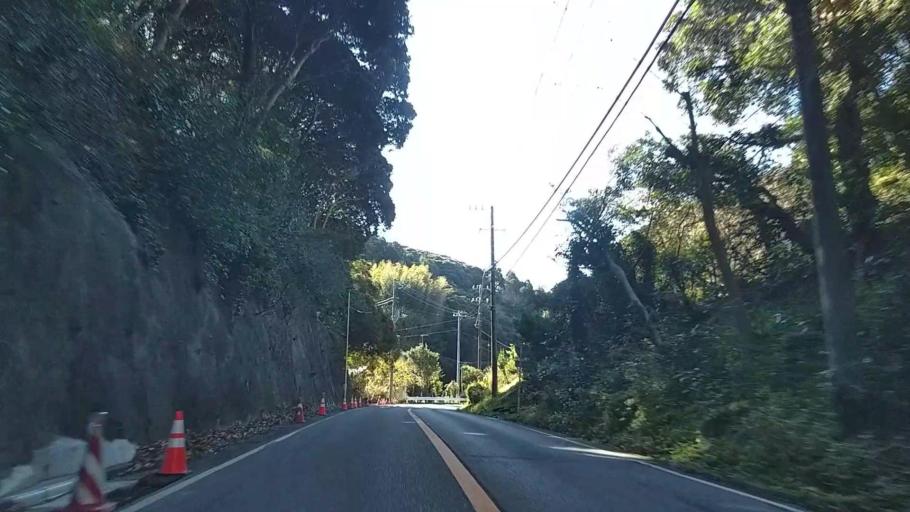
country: JP
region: Chiba
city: Tateyama
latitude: 34.9601
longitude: 139.8545
